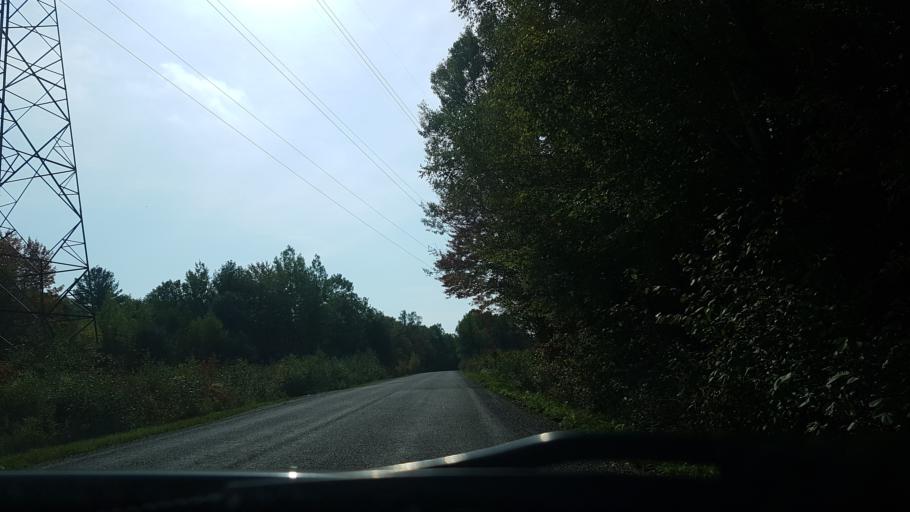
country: CA
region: Ontario
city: Gravenhurst
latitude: 44.8096
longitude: -79.2119
